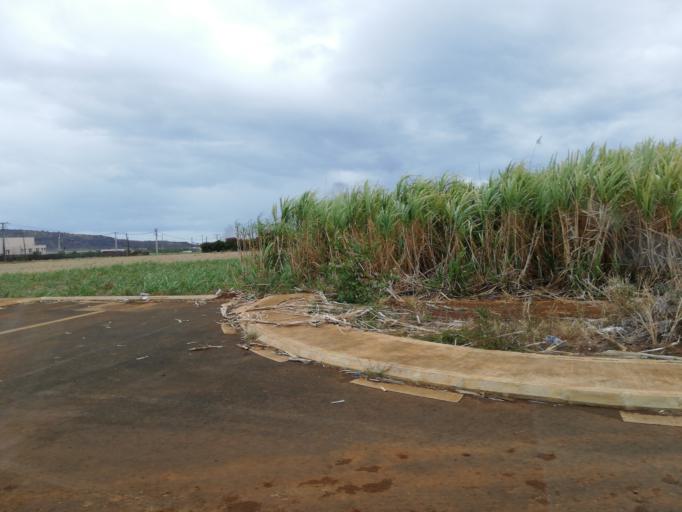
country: MU
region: Black River
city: Petite Riviere
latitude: -20.2134
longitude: 57.4623
